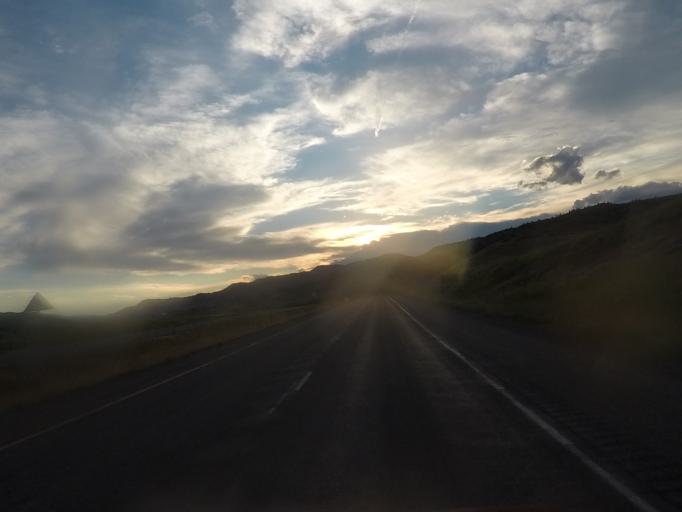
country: US
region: Montana
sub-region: Park County
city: Livingston
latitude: 45.6565
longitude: -110.6276
